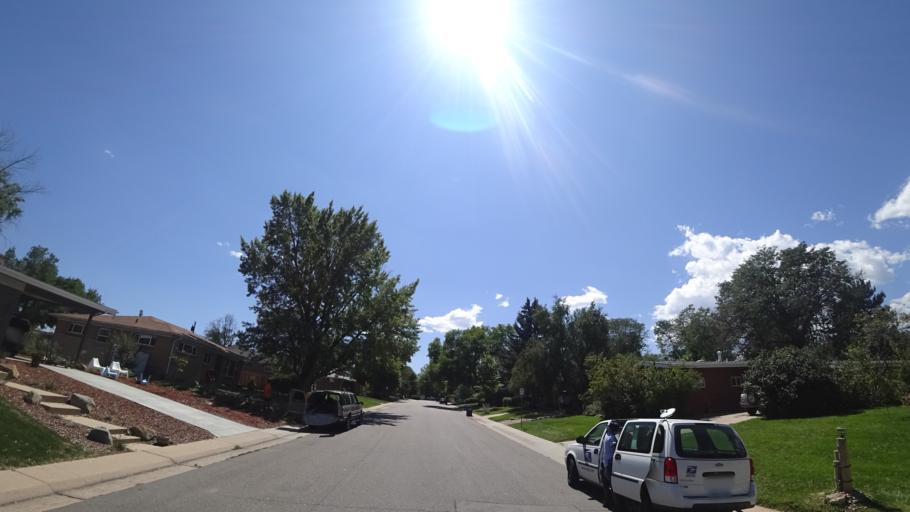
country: US
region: Colorado
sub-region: Arapahoe County
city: Littleton
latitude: 39.6082
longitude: -104.9892
